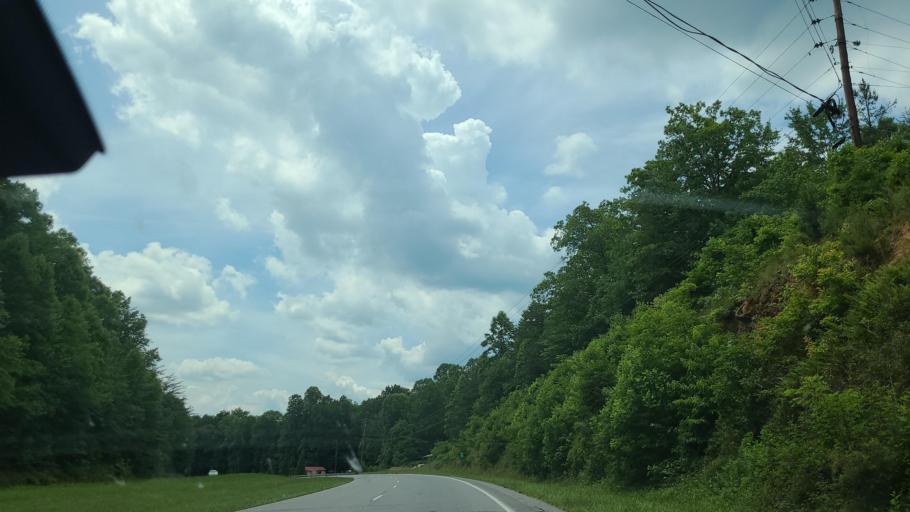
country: US
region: Georgia
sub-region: Fannin County
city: McCaysville
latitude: 35.0213
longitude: -84.2491
